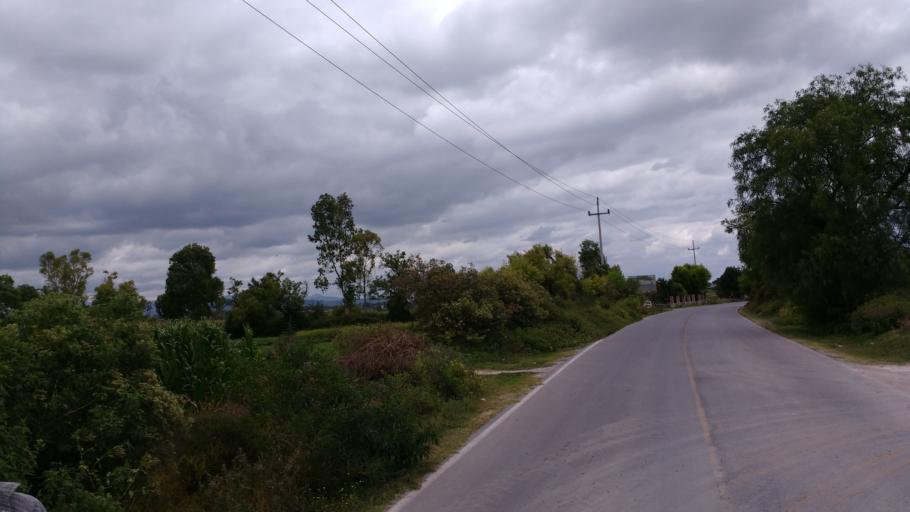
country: MX
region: Hidalgo
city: Mixquiahuala de Juarez
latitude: 20.2432
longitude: -99.2448
